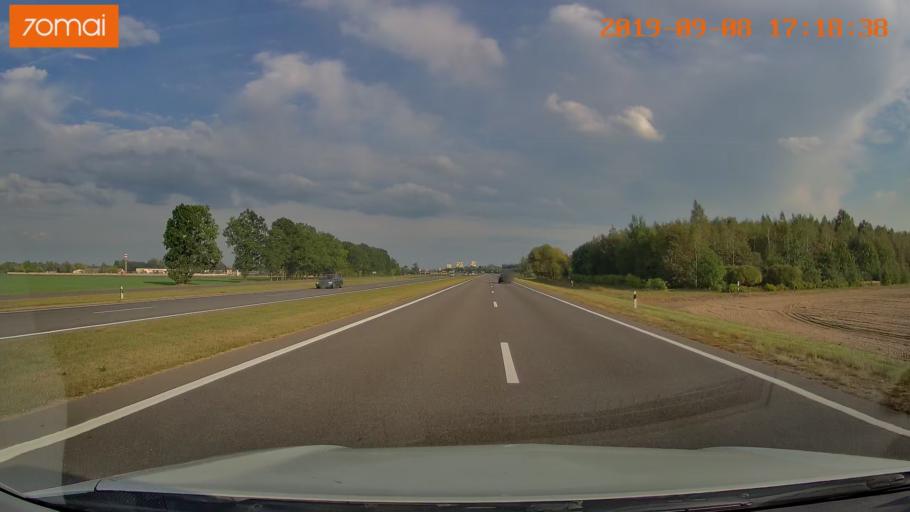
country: BY
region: Grodnenskaya
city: Skidal'
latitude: 53.5856
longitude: 24.1772
